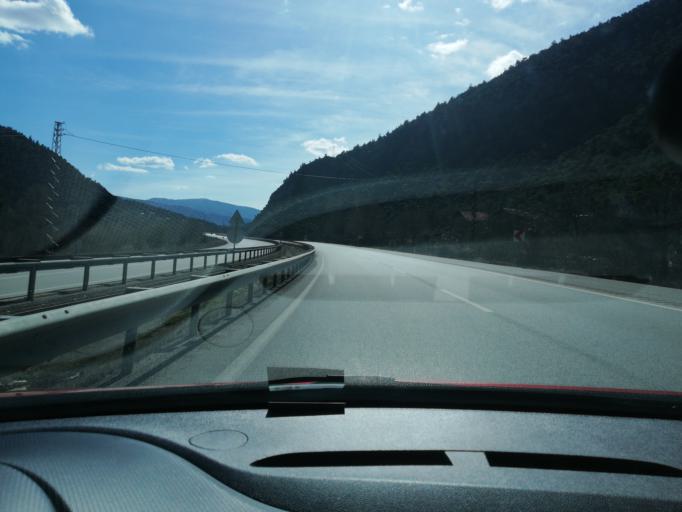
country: TR
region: Karabuk
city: Eskipazar
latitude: 41.0509
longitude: 32.6414
